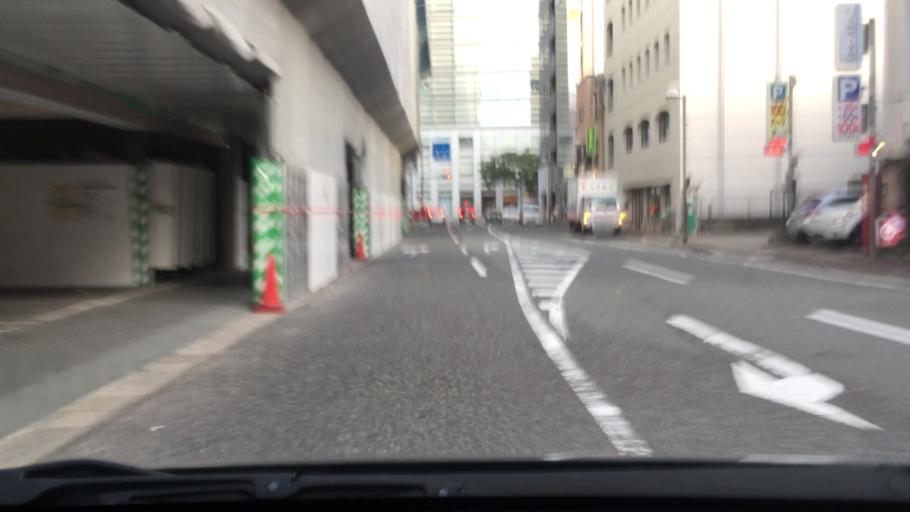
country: JP
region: Fukuoka
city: Fukuoka-shi
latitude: 33.5931
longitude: 130.4021
